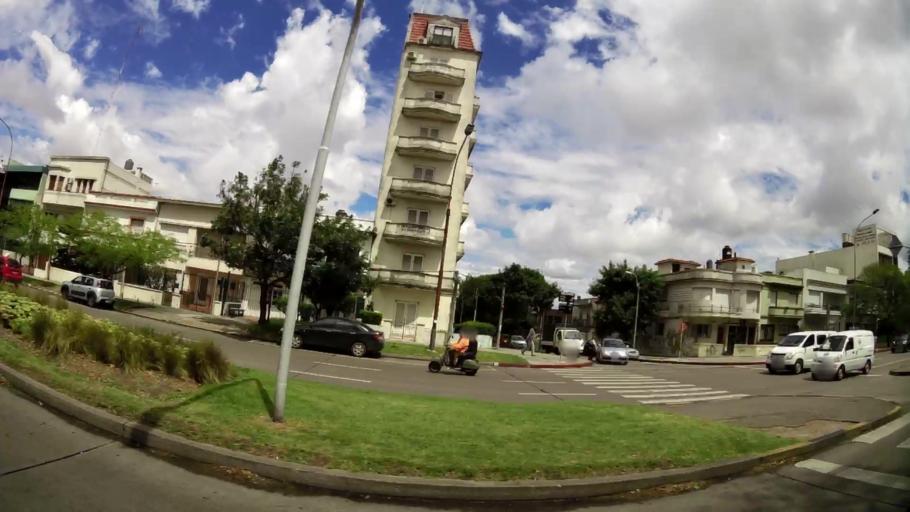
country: UY
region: Montevideo
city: Montevideo
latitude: -34.8870
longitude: -56.1657
